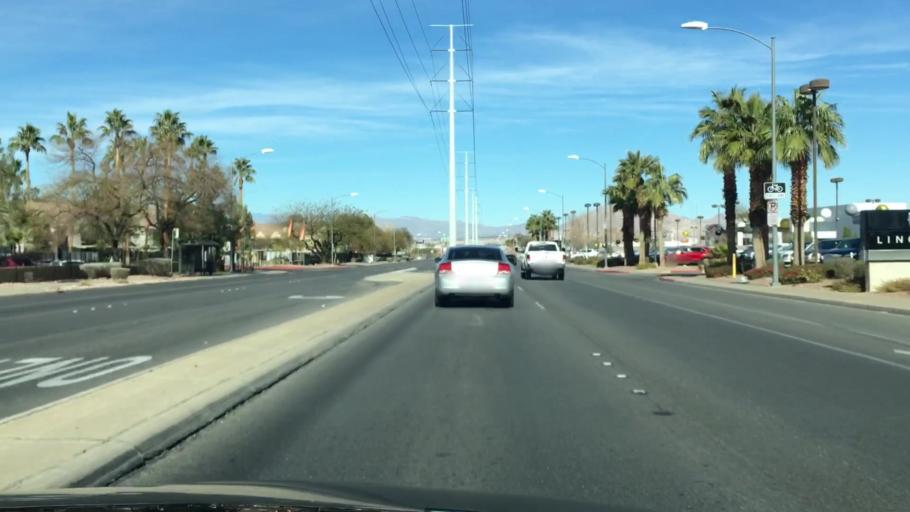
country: US
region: Nevada
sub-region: Clark County
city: Henderson
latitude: 36.0501
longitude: -115.0289
